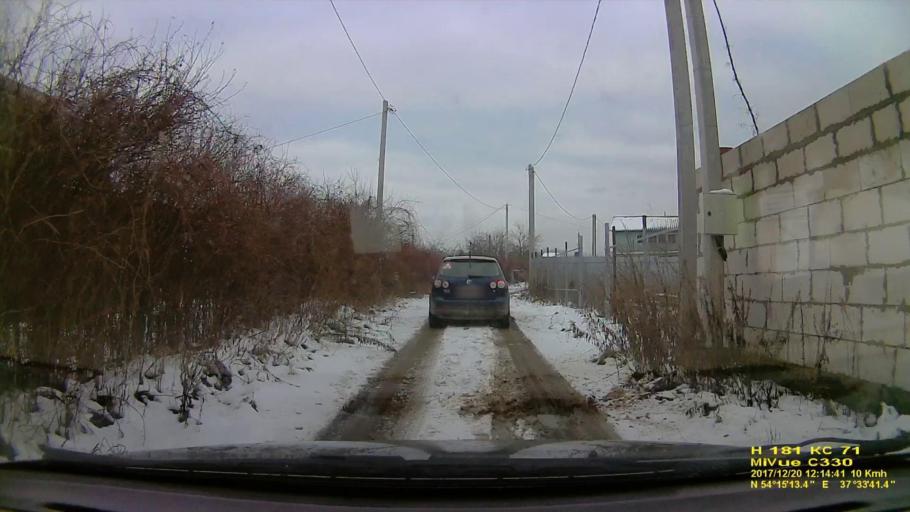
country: RU
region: Tula
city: Gorelki
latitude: 54.2537
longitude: 37.5615
